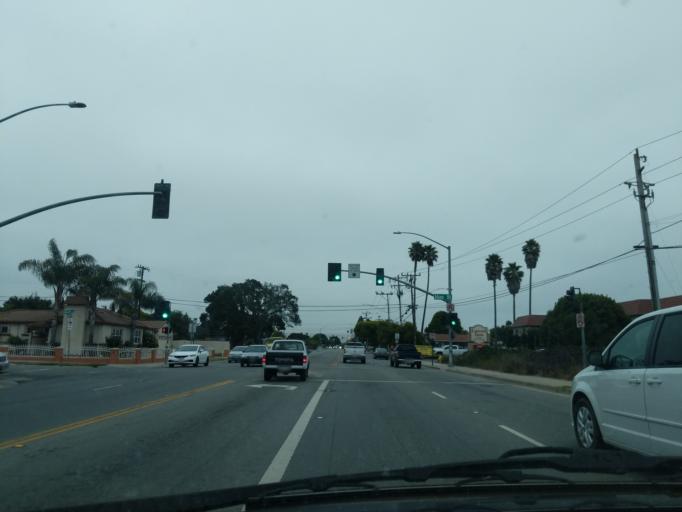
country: US
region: California
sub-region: Monterey County
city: Boronda
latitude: 36.6979
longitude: -121.6627
